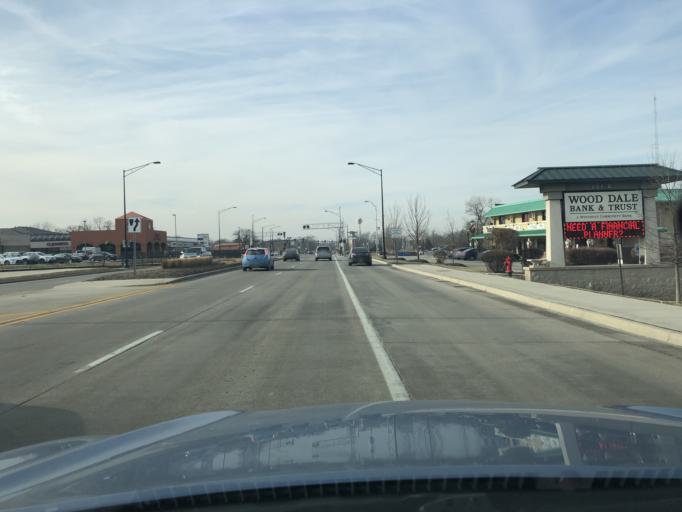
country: US
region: Illinois
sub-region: DuPage County
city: Wood Dale
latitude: 41.9631
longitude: -87.9759
